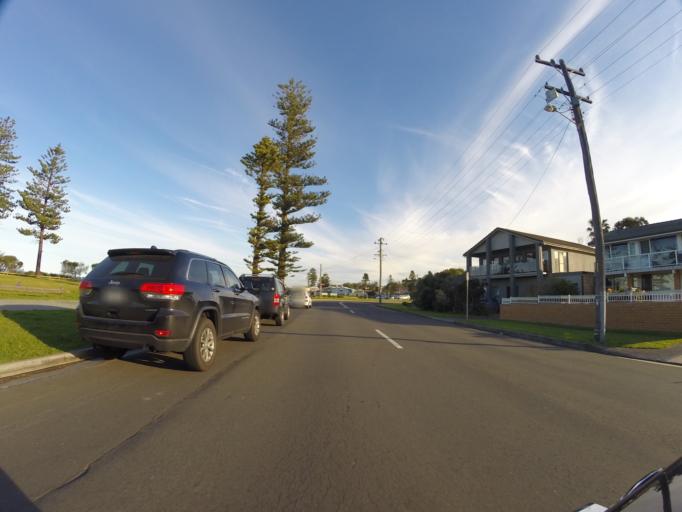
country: AU
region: New South Wales
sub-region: Wollongong
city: Bulli
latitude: -34.3394
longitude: 150.9244
